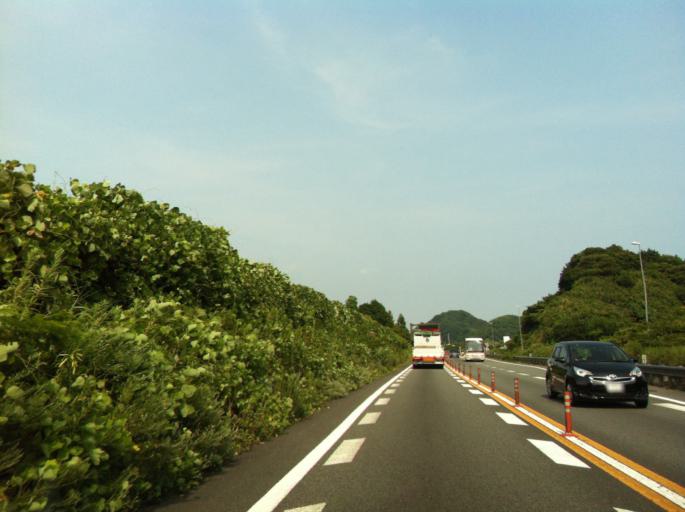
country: JP
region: Shizuoka
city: Fujieda
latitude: 34.8688
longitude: 138.2179
